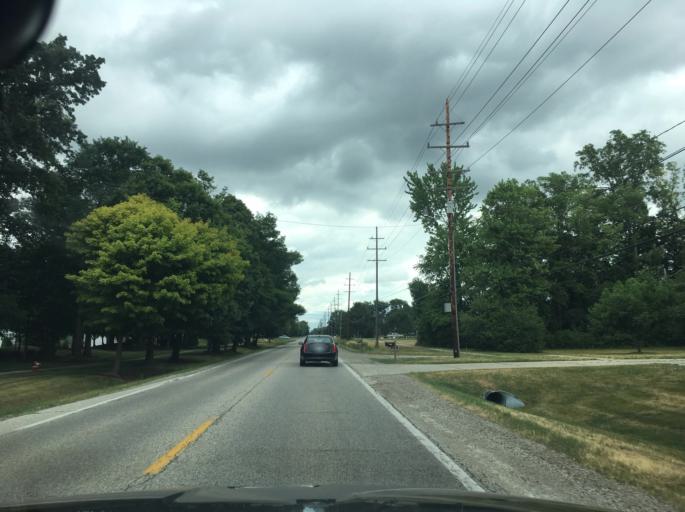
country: US
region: Michigan
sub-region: Macomb County
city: Shelby
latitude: 42.6553
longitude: -83.0100
